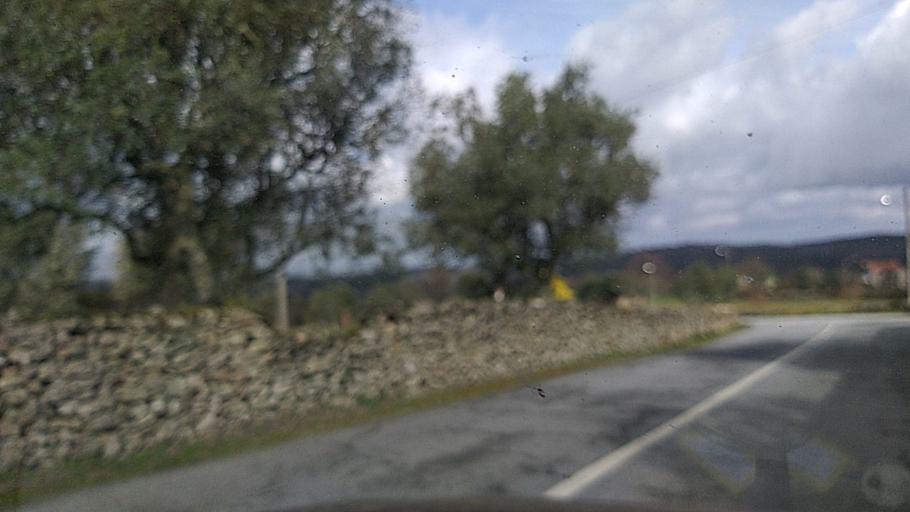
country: PT
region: Guarda
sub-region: Fornos de Algodres
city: Fornos de Algodres
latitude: 40.6519
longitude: -7.5490
